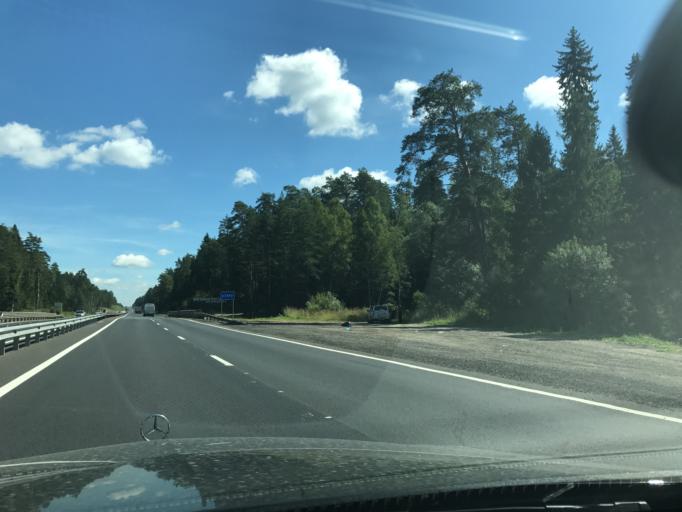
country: RU
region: Vladimir
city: Stepantsevo
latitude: 56.2287
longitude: 41.6929
